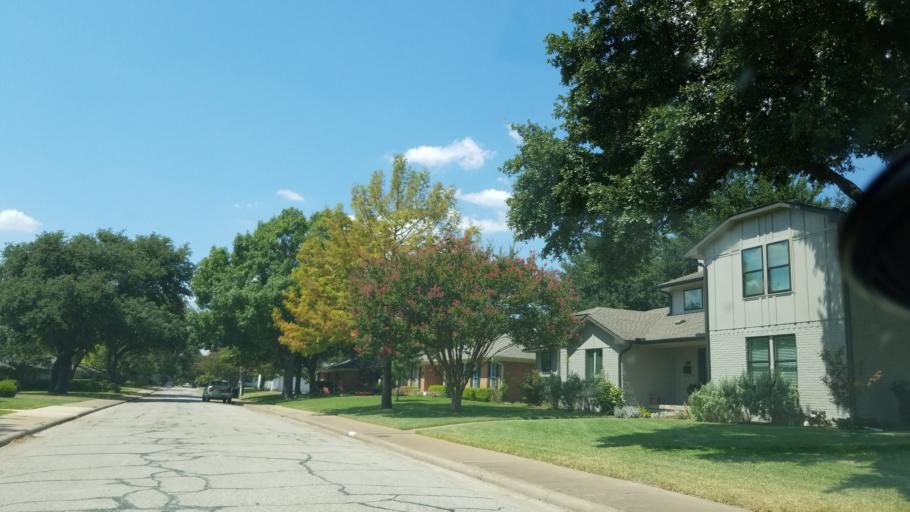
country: US
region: Texas
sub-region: Dallas County
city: Richardson
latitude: 32.8896
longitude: -96.7093
